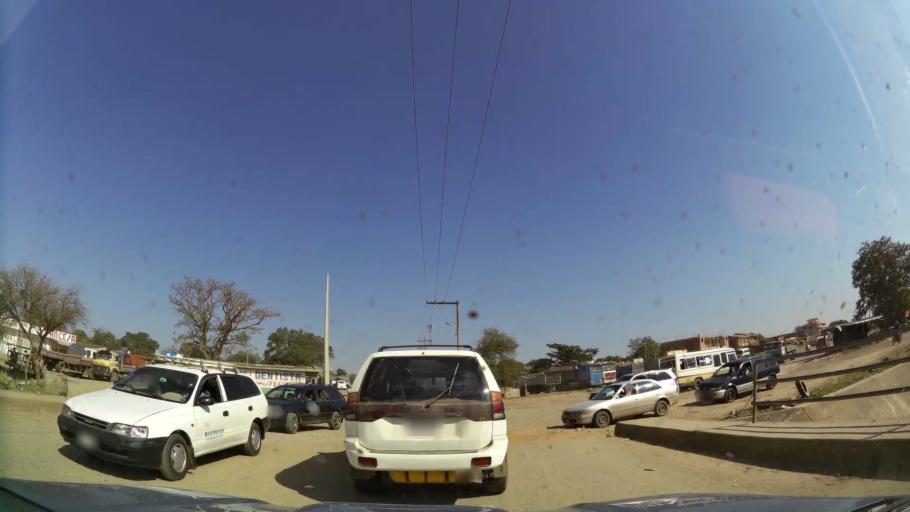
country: BO
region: Santa Cruz
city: Cotoca
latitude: -17.8137
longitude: -63.1100
